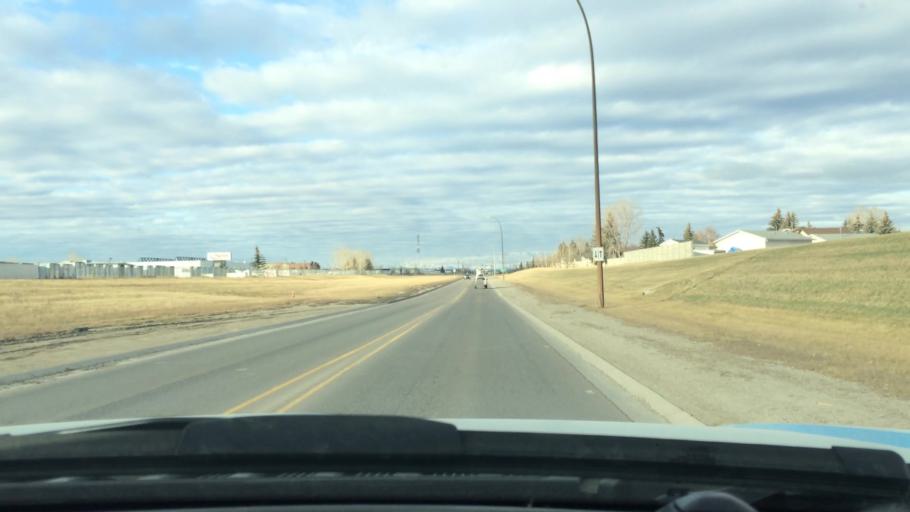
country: CA
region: Alberta
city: Calgary
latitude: 51.0150
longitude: -113.9686
